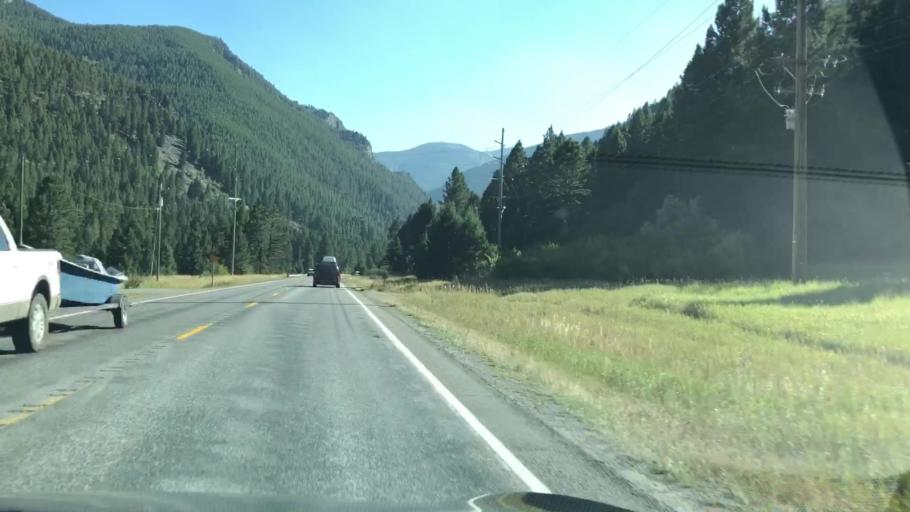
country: US
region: Montana
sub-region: Gallatin County
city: Four Corners
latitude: 45.4392
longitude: -111.2339
